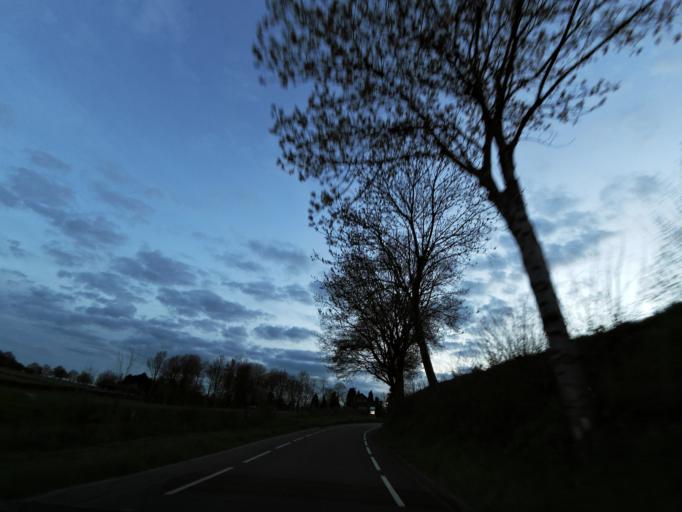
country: NL
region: Limburg
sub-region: Gemeente Voerendaal
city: Ubachsberg
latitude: 50.8528
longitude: 5.9563
